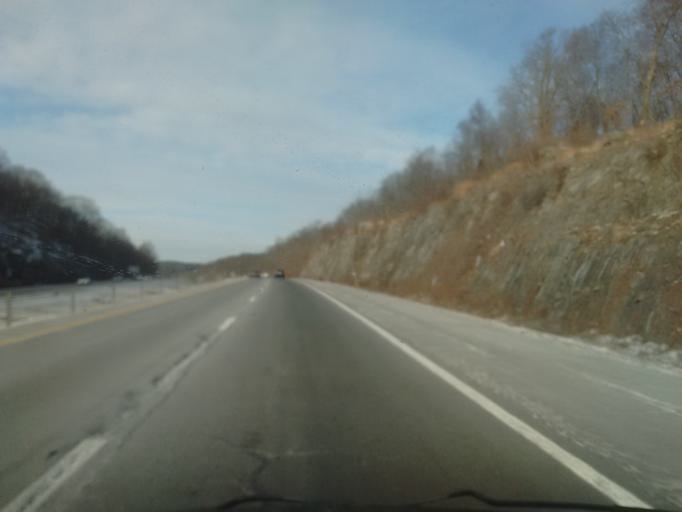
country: US
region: New York
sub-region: Putnam County
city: Brewster Hill
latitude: 41.4386
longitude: -73.6315
